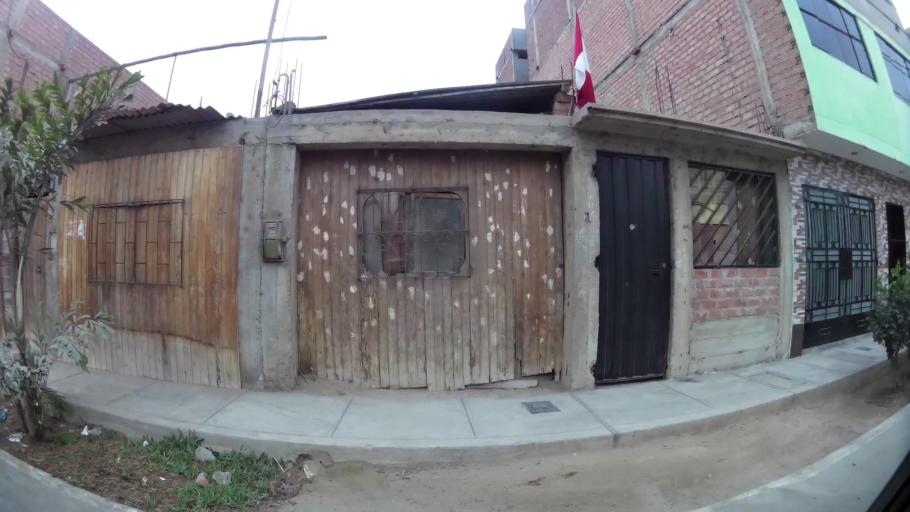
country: PE
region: Lima
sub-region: Lima
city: Urb. Santo Domingo
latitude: -11.8902
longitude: -77.0641
